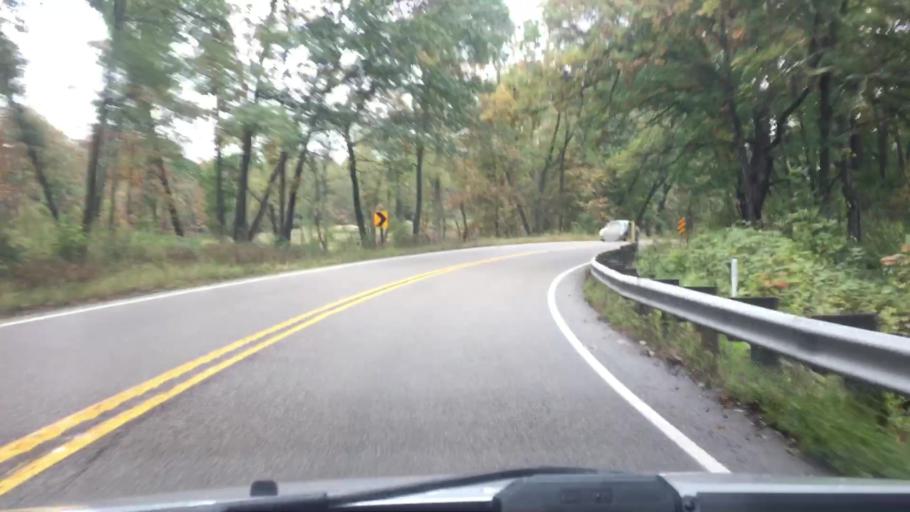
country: US
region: Wisconsin
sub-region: Waukesha County
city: Eagle
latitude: 42.9324
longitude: -88.4645
